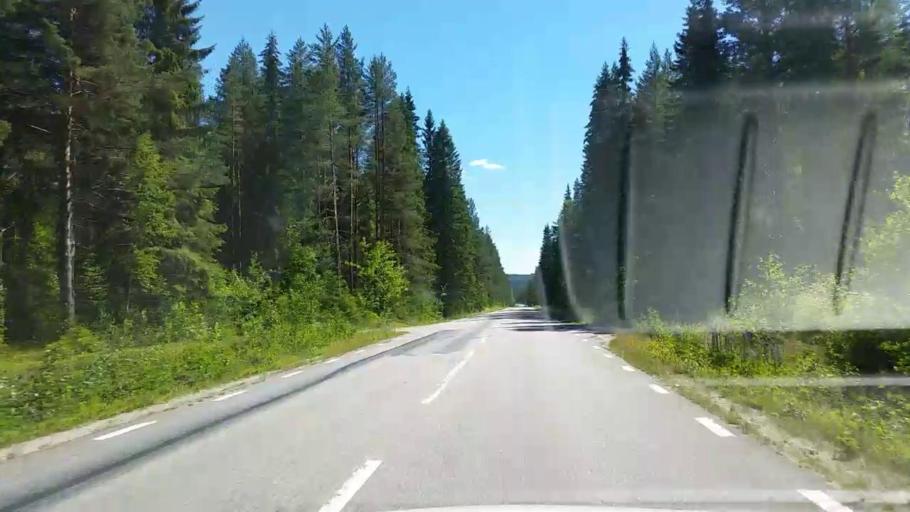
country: SE
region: Gaevleborg
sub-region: Ovanakers Kommun
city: Edsbyn
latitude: 61.3497
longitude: 15.8157
